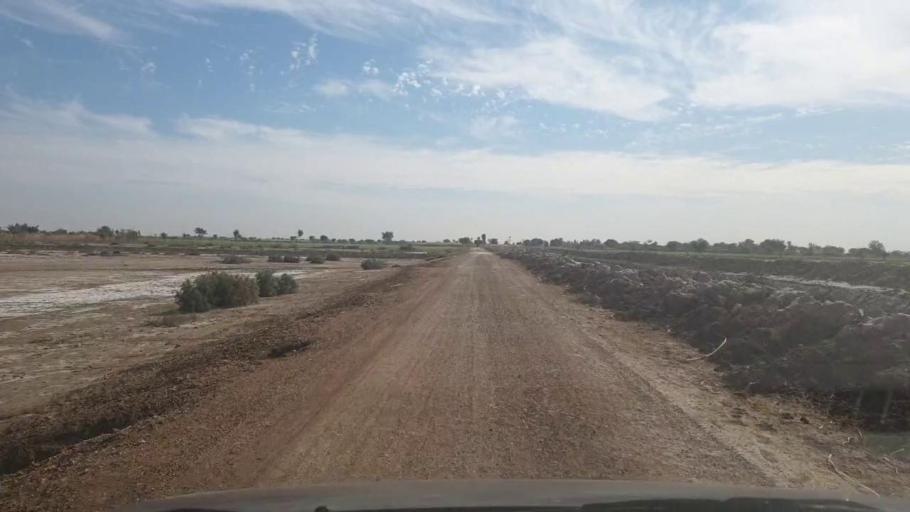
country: PK
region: Sindh
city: Mirwah Gorchani
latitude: 25.4236
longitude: 69.2008
